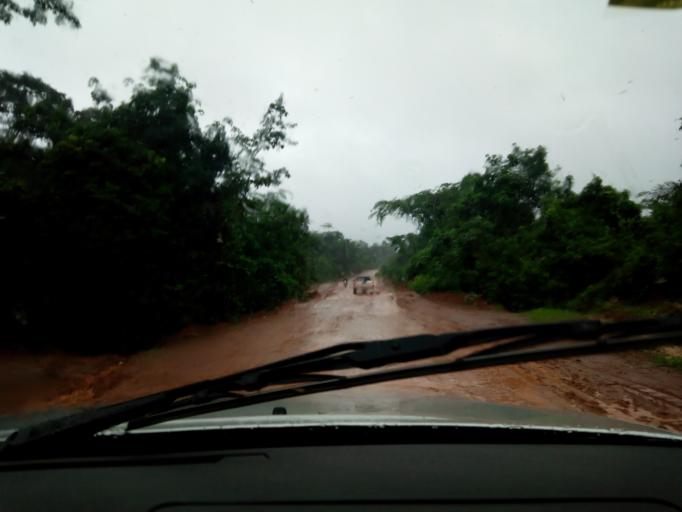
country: LR
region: Nimba
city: Sanniquellie
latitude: 7.1085
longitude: -8.9246
